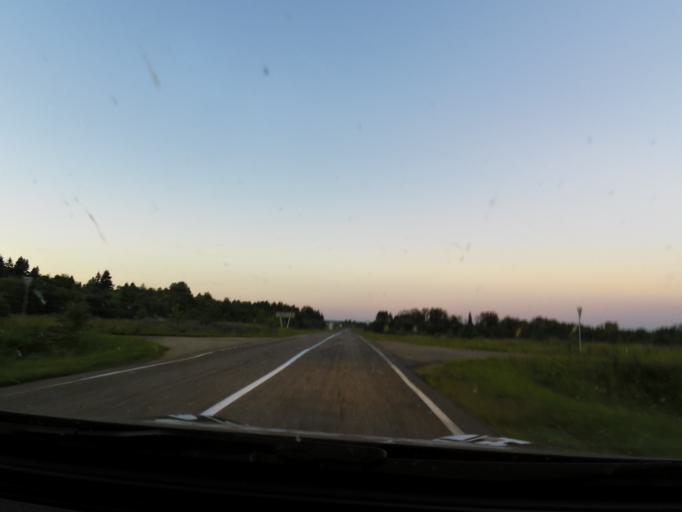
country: RU
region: Kostroma
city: Buy
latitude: 58.3514
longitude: 41.1699
